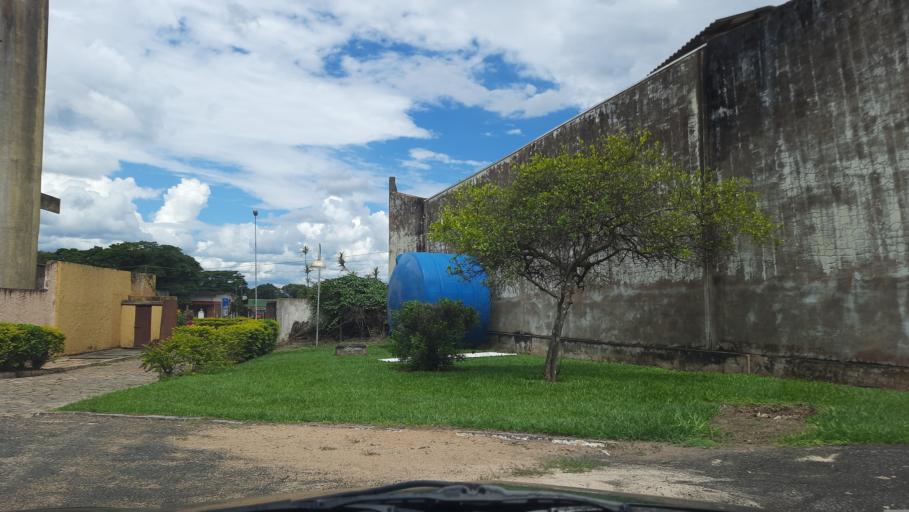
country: BR
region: Sao Paulo
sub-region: Casa Branca
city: Casa Branca
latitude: -21.7828
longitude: -47.0638
